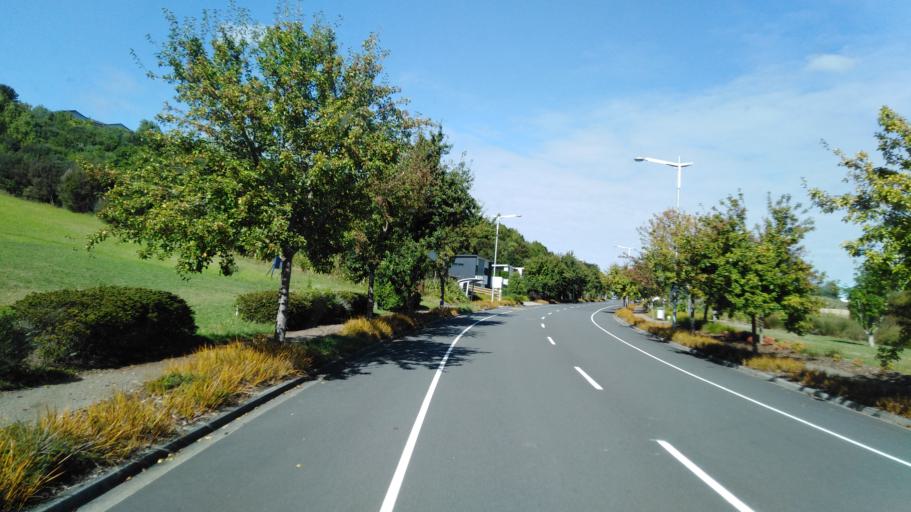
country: NZ
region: Bay of Plenty
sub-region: Tauranga City
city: Tauranga
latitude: -37.7493
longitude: 176.1088
